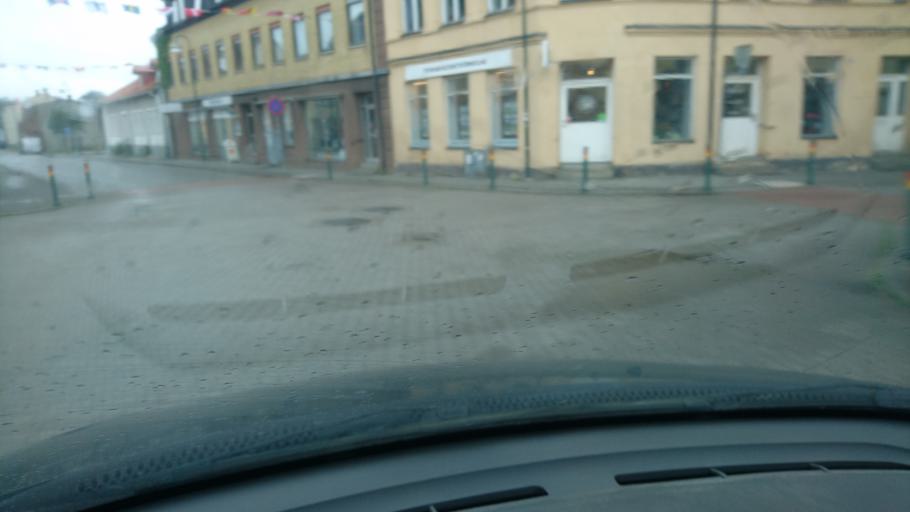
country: SE
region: Skane
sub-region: Tomelilla Kommun
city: Tomelilla
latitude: 55.5444
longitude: 13.9499
